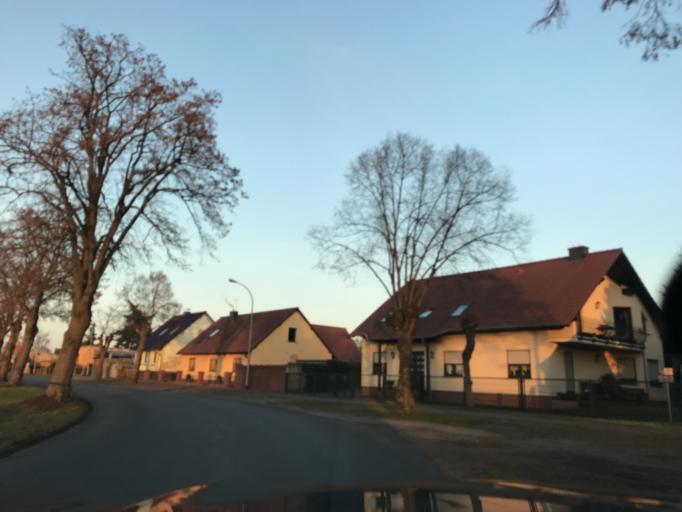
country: DE
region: Brandenburg
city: Wusterwitz
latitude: 52.4723
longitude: 12.4540
